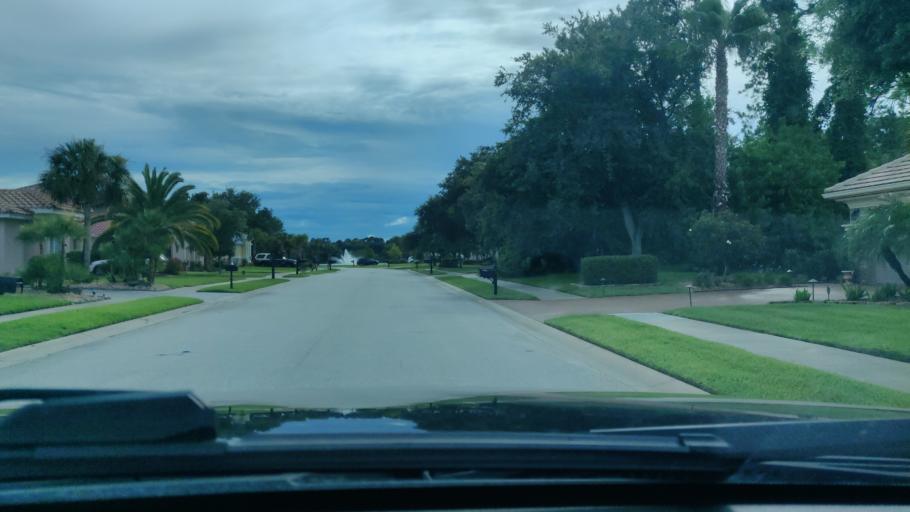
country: US
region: Florida
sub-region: Flagler County
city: Flagler Beach
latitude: 29.5224
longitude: -81.1599
